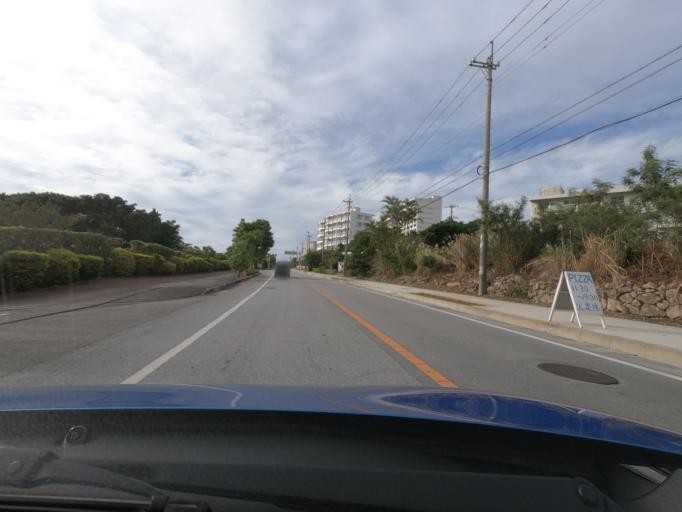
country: JP
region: Okinawa
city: Nago
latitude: 26.6811
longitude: 127.8854
